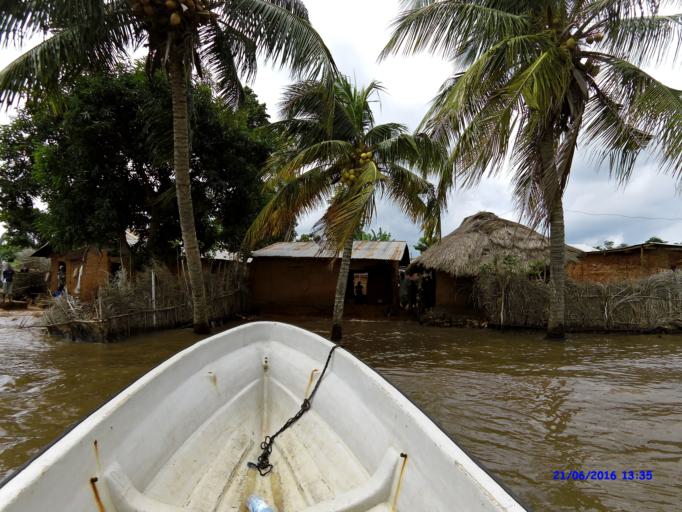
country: BJ
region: Mono
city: Come
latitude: 6.5050
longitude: 2.0009
